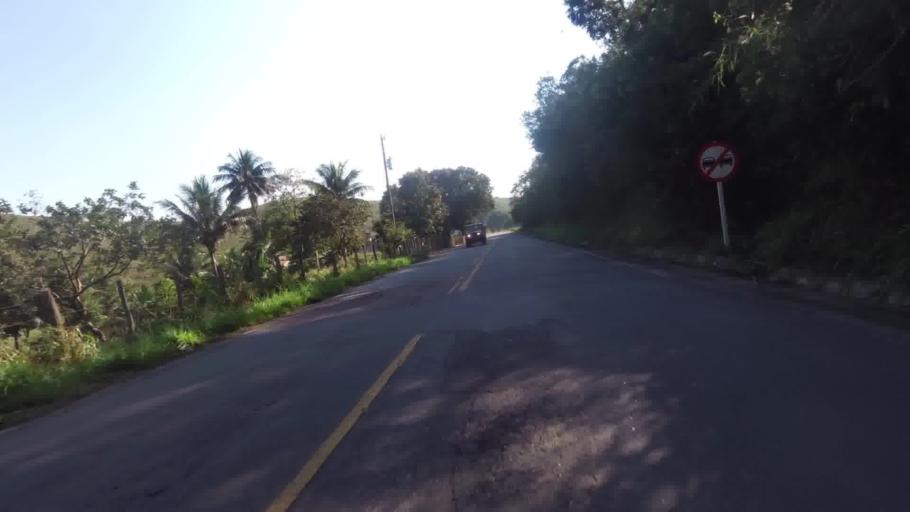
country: BR
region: Espirito Santo
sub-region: Alfredo Chaves
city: Alfredo Chaves
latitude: -20.6850
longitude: -40.7067
